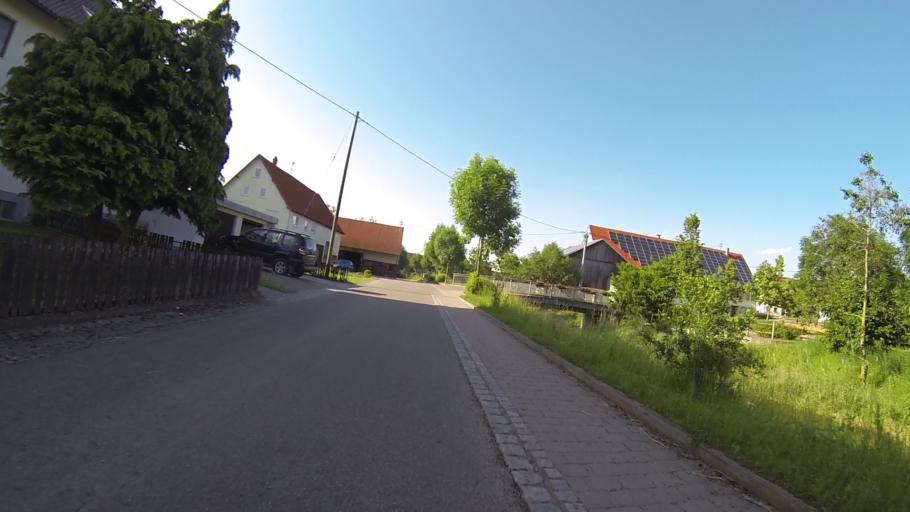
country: DE
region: Baden-Wuerttemberg
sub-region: Tuebingen Region
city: Mietingen
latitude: 48.1717
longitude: 9.8641
